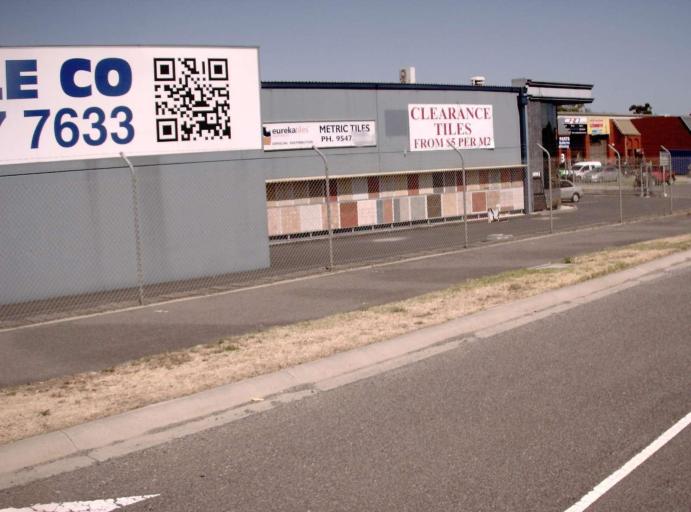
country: AU
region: Victoria
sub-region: Greater Dandenong
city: Springvale
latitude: -37.9414
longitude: 145.1404
